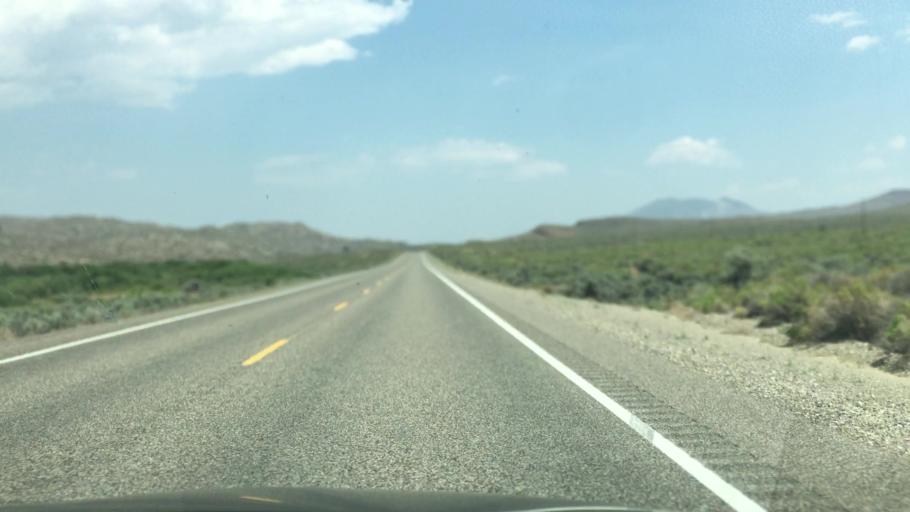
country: US
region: Nevada
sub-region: Elko County
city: Jackpot
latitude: 41.7268
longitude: -114.7968
